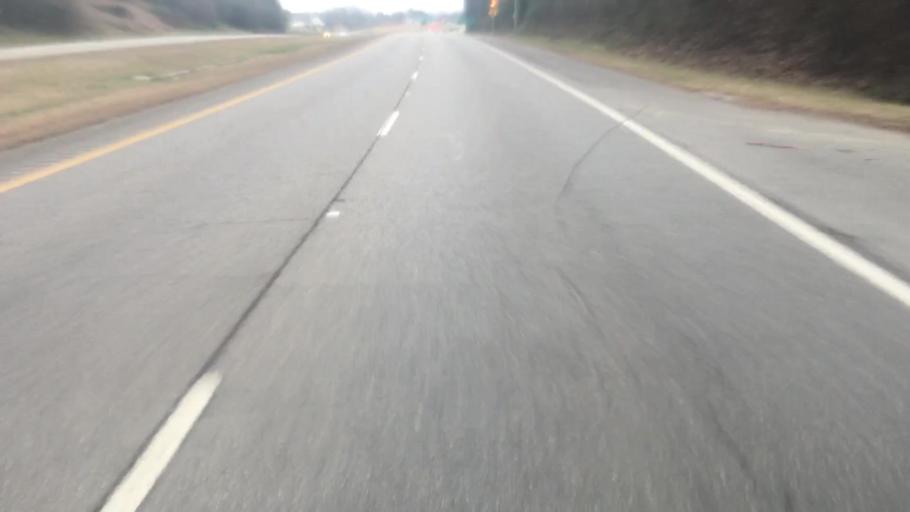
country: US
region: Alabama
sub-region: Walker County
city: Sumiton
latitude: 33.7476
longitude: -87.0542
